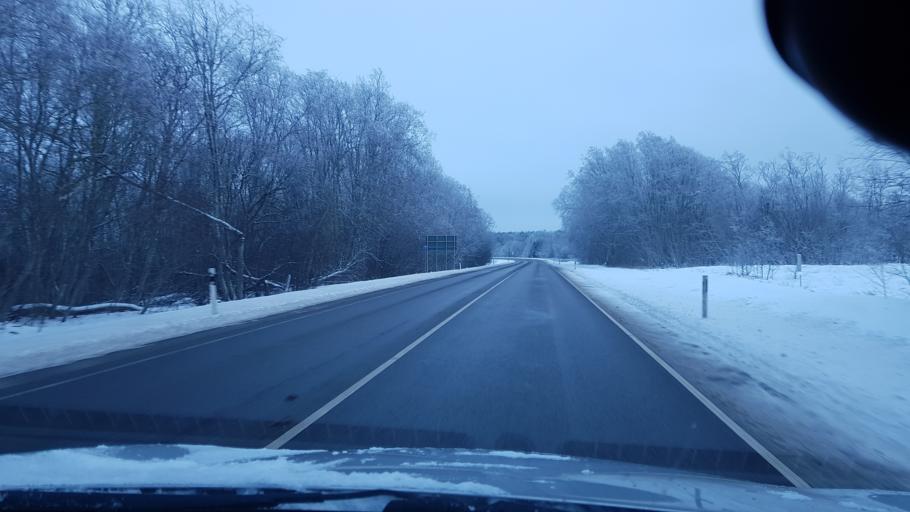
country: EE
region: Harju
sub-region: Paldiski linn
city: Paldiski
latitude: 59.3414
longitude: 24.1988
